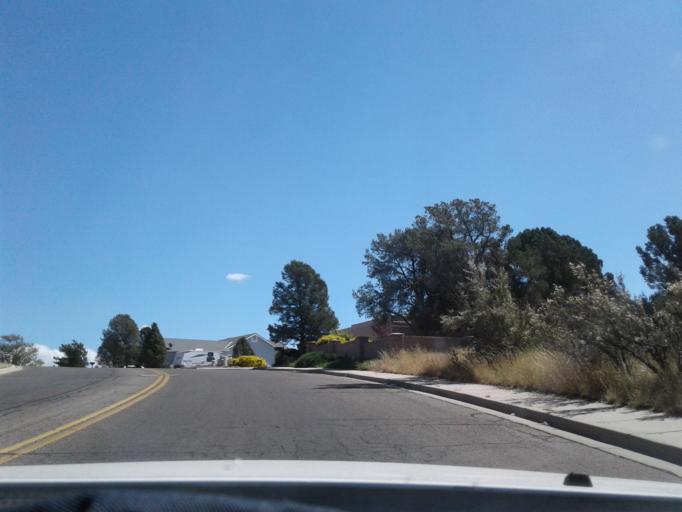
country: US
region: Arizona
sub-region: Yavapai County
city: Prescott
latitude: 34.5692
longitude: -112.4707
